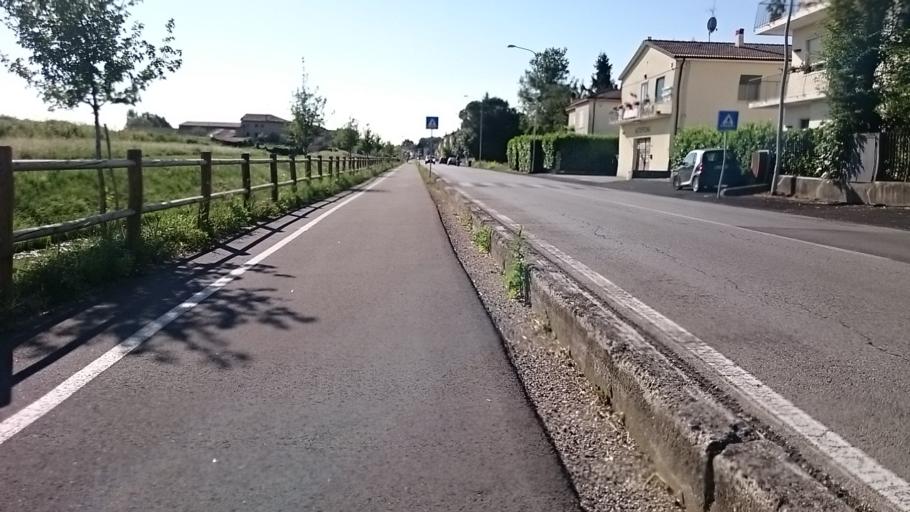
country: IT
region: Veneto
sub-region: Provincia di Vicenza
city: Arcugnano-Torri
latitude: 45.5003
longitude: 11.5786
